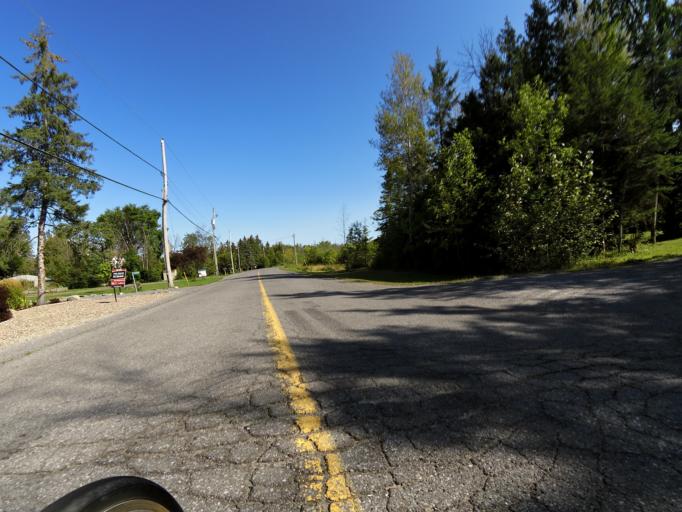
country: CA
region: Ontario
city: Bells Corners
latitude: 45.4749
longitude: -75.9926
